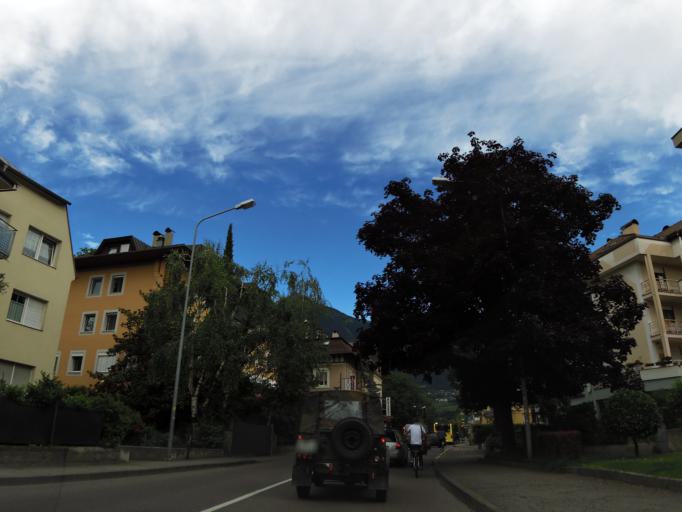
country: IT
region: Trentino-Alto Adige
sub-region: Bolzano
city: Merano
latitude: 46.6633
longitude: 11.1594
